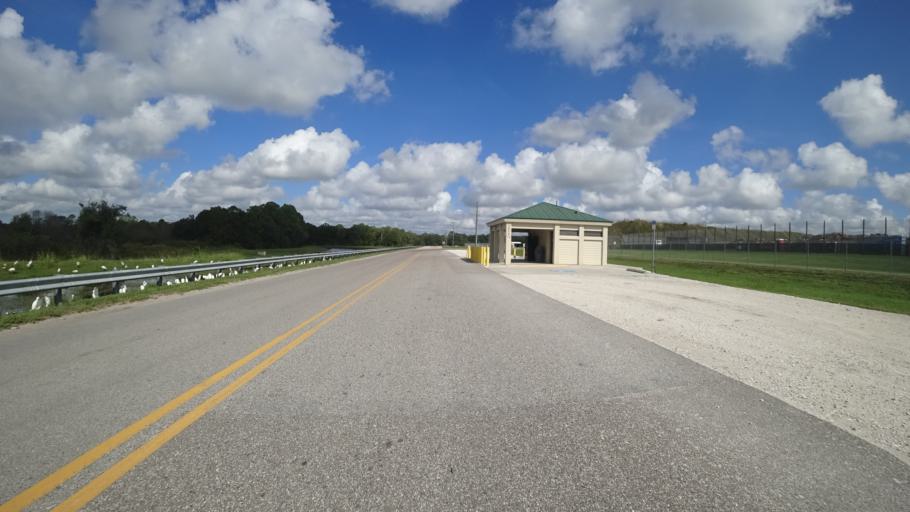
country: US
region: Florida
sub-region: Manatee County
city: Ellenton
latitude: 27.4753
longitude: -82.4466
